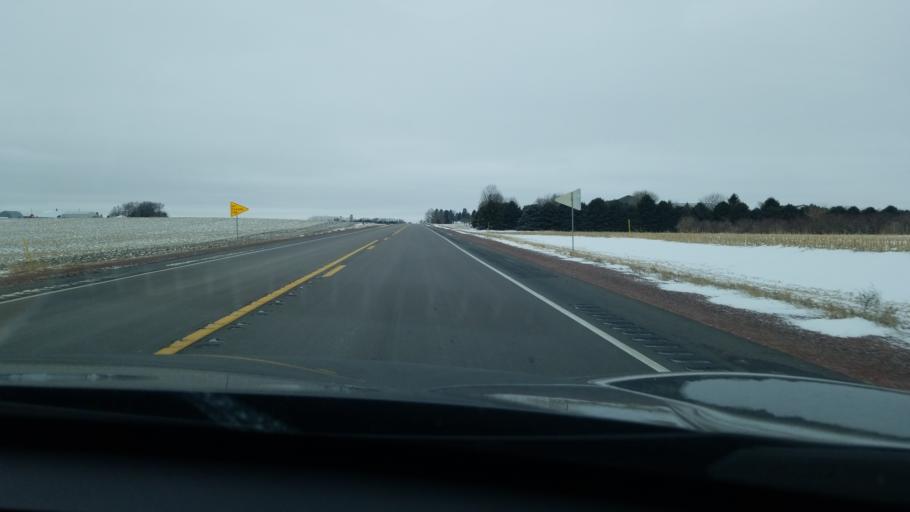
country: US
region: Iowa
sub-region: Lyon County
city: Rock Rapids
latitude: 43.4330
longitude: -96.3705
